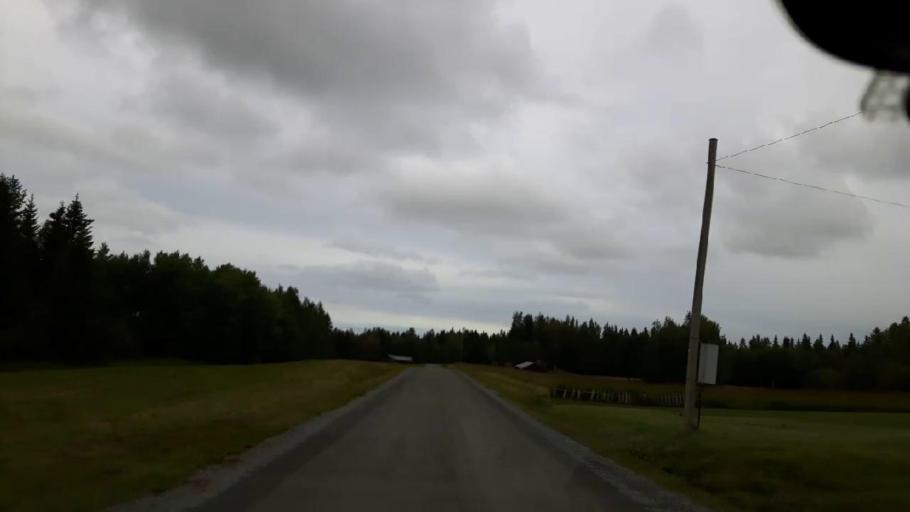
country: SE
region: Jaemtland
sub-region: OEstersunds Kommun
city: Ostersund
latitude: 63.0939
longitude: 14.5507
